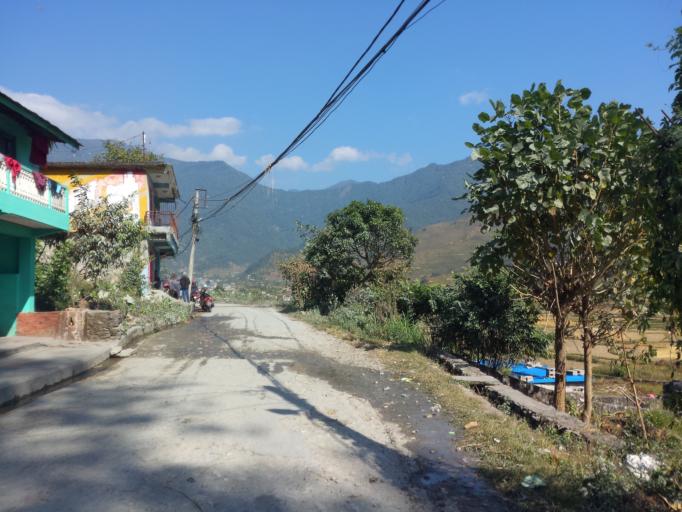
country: NP
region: Western Region
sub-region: Gandaki Zone
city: Pokhara
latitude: 28.2728
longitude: 83.9803
